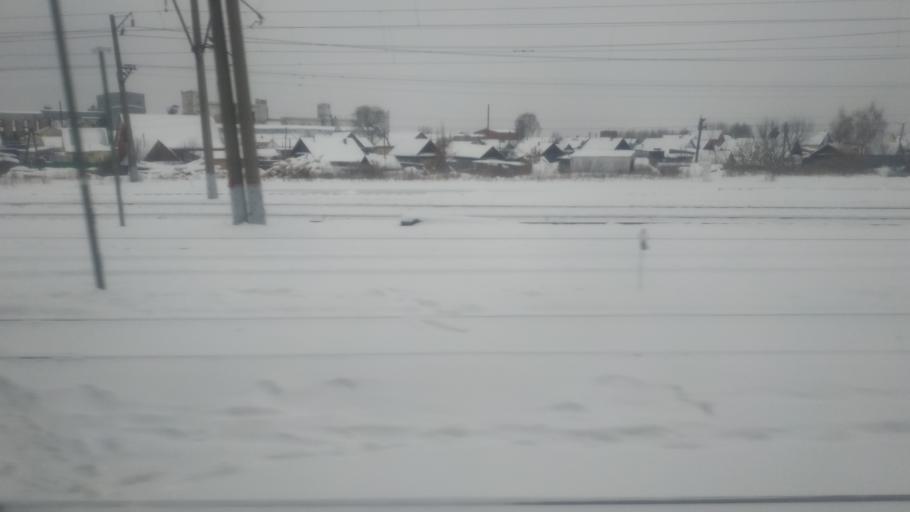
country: RU
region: Bashkortostan
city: Yanaul
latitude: 56.2750
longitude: 54.9387
